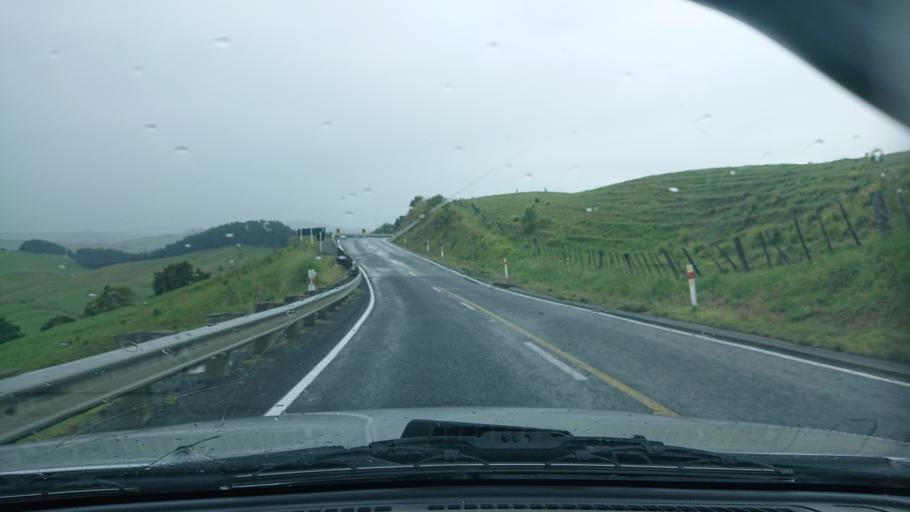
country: NZ
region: Auckland
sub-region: Auckland
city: Wellsford
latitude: -36.3546
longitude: 174.4707
